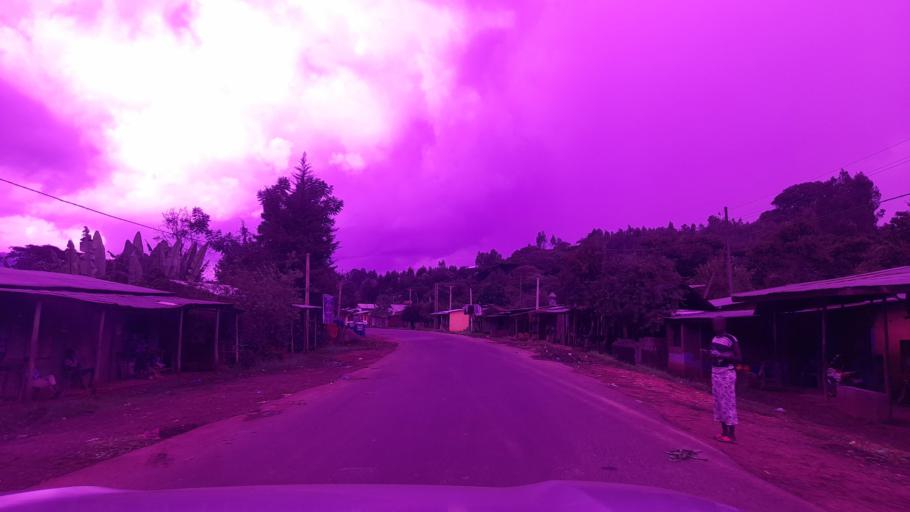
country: ET
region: Oromiya
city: Jima
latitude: 7.6670
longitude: 36.8916
